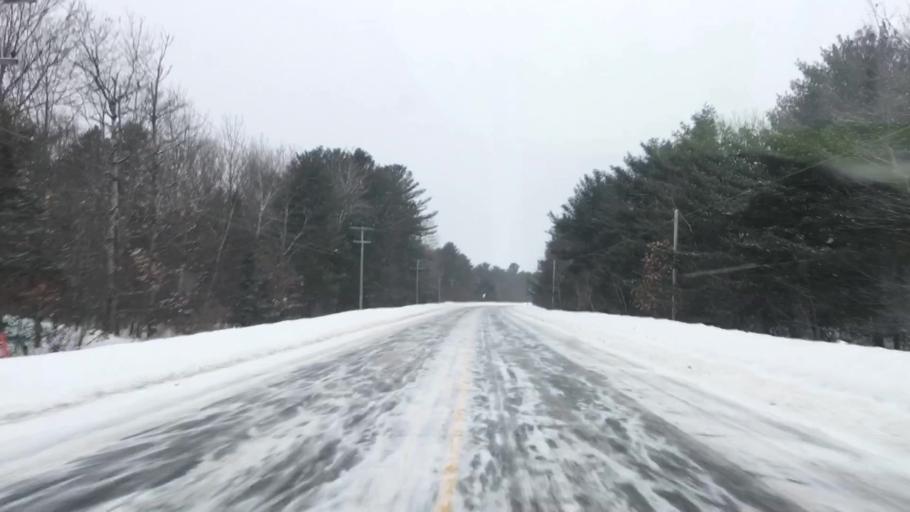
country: US
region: Maine
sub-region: Penobscot County
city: Medway
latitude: 45.5633
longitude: -68.3963
